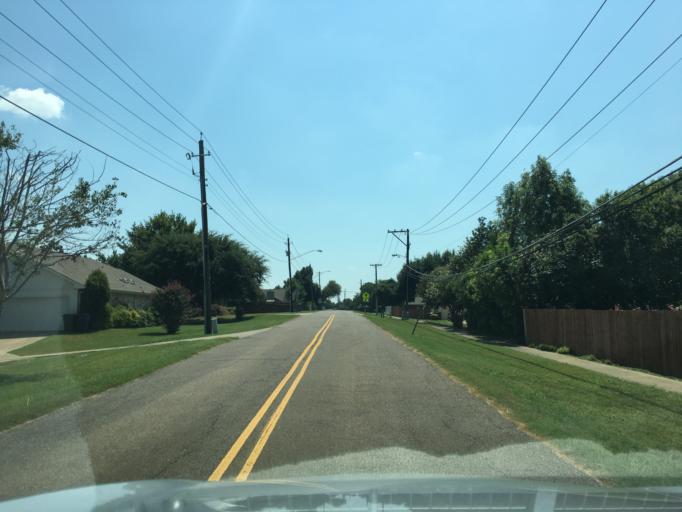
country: US
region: Texas
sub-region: Collin County
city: Plano
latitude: 32.9698
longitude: -96.6701
